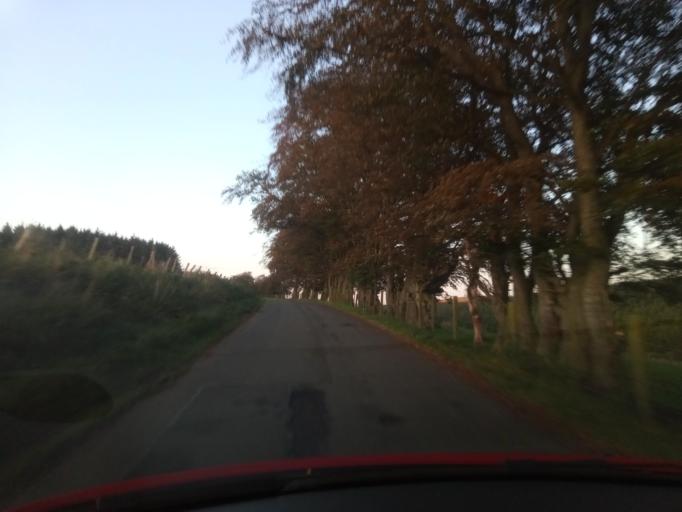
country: GB
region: Scotland
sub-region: Fife
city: Pathhead
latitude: 55.7924
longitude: -2.8903
